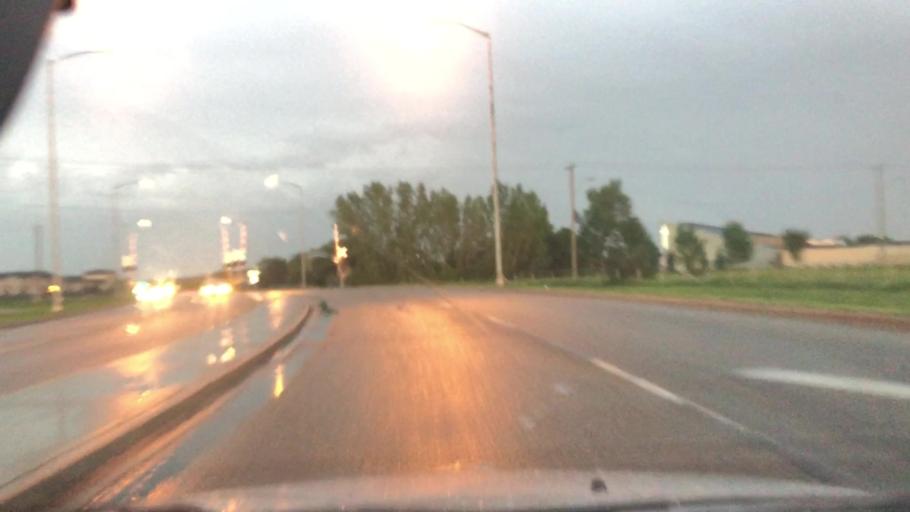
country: CA
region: Alberta
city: St. Albert
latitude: 53.6288
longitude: -113.5669
